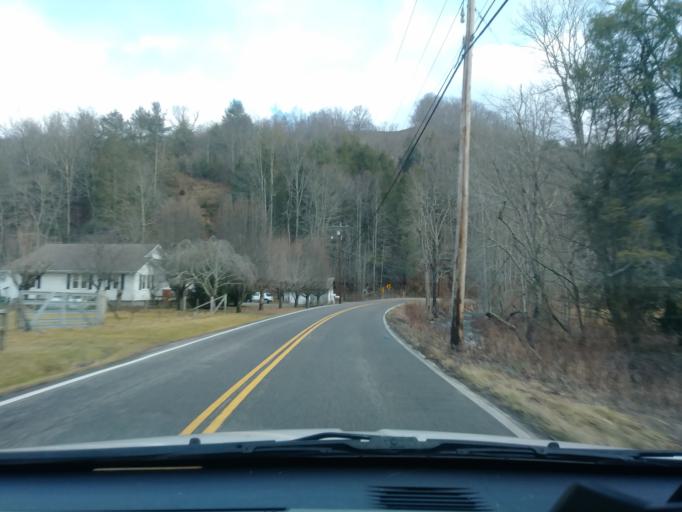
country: US
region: Tennessee
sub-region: Carter County
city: Elizabethton
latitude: 36.2204
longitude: -82.1993
